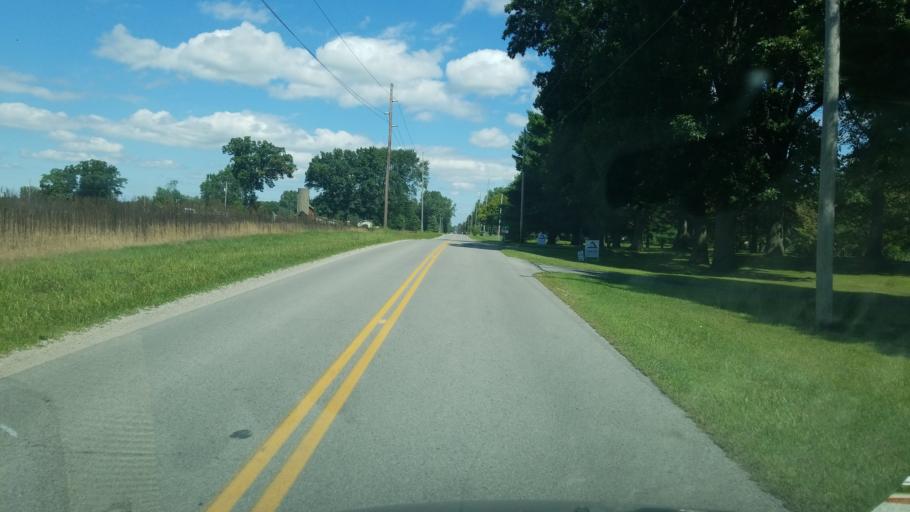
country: US
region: Ohio
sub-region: Henry County
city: Liberty Center
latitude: 41.4565
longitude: -83.9214
